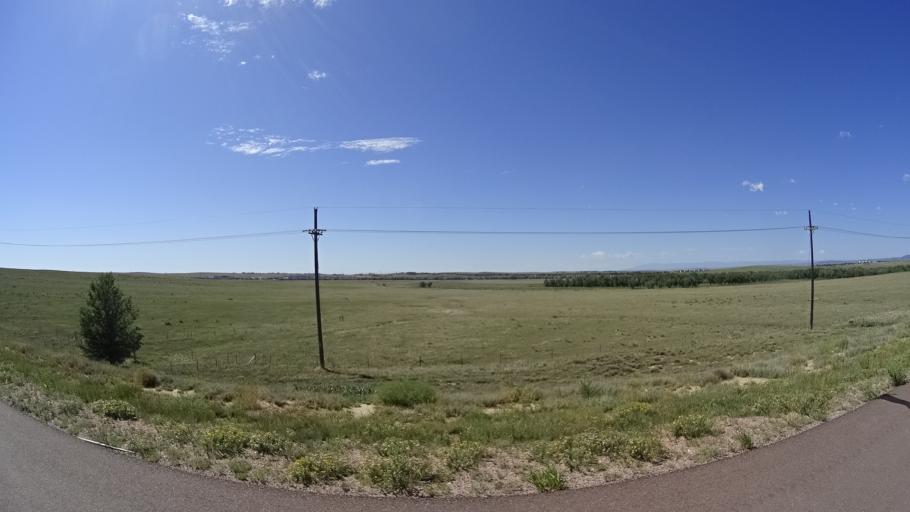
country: US
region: Colorado
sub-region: El Paso County
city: Security-Widefield
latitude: 38.7615
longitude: -104.6418
